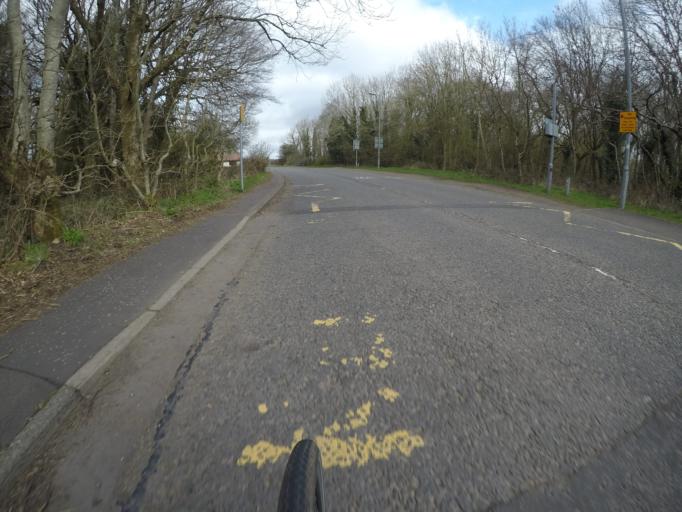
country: GB
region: Scotland
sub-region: North Ayrshire
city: Irvine
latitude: 55.6341
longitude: -4.6331
